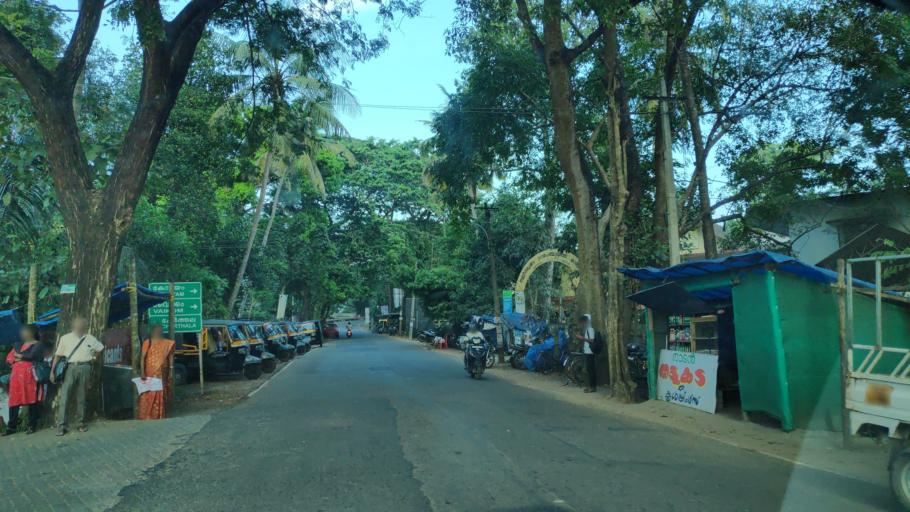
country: IN
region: Kerala
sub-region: Alappuzha
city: Shertallai
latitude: 9.6760
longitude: 76.3921
